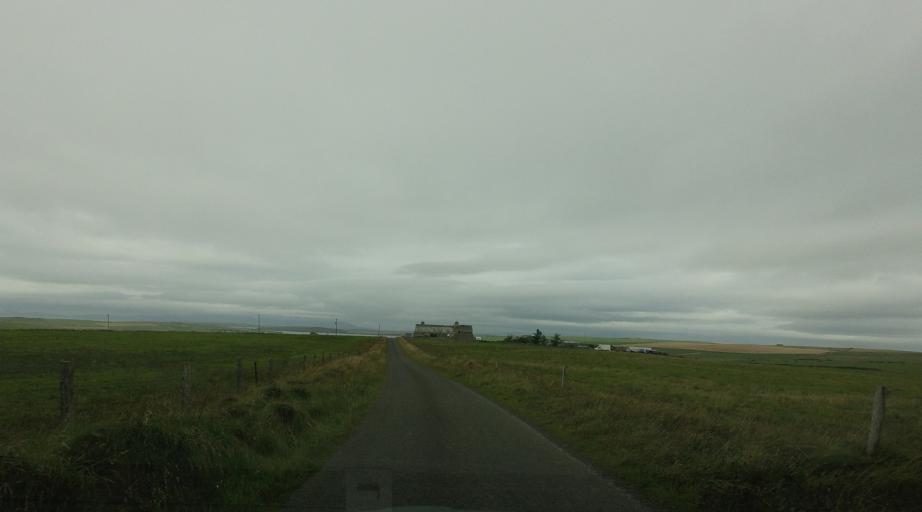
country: GB
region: Scotland
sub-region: Orkney Islands
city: Orkney
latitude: 58.8018
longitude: -2.9554
